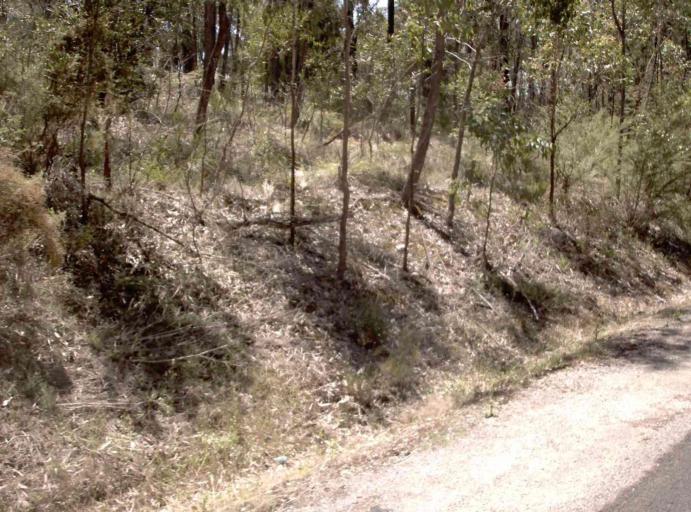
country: AU
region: Victoria
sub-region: East Gippsland
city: Lakes Entrance
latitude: -37.6925
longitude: 148.6146
